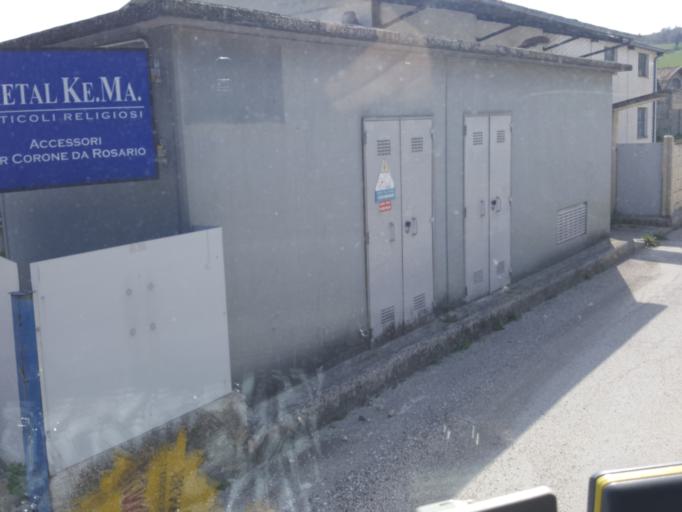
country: IT
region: The Marches
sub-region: Provincia di Ancona
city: Loreto Stazione
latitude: 43.4399
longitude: 13.6300
